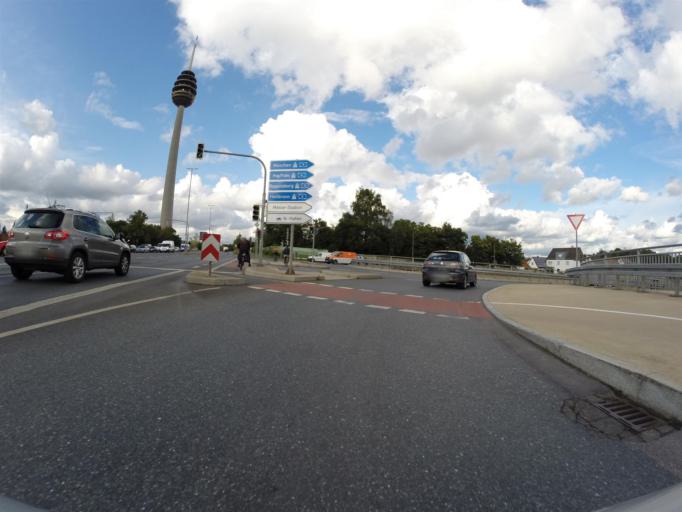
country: DE
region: Bavaria
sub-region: Regierungsbezirk Mittelfranken
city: Grossreuth bei Schweinau
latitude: 49.4227
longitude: 11.0378
